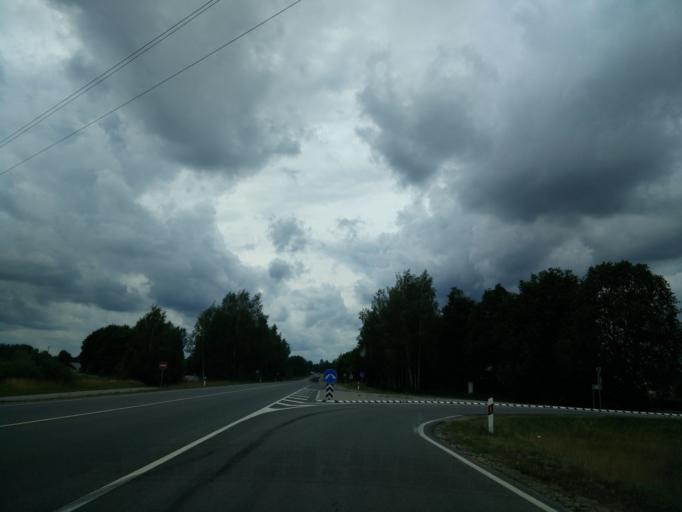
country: LT
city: Trakai
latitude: 54.6273
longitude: 24.9594
